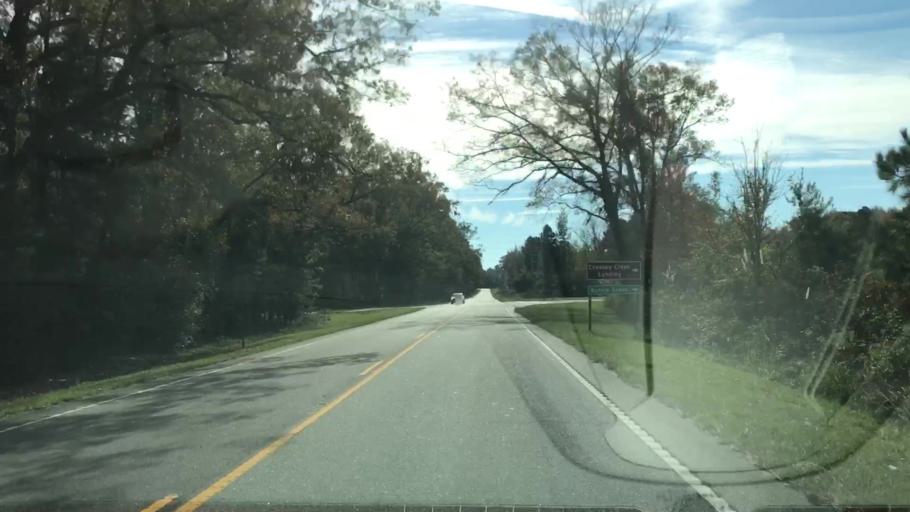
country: US
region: South Carolina
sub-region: Colleton County
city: Walterboro
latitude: 32.8430
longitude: -80.5897
